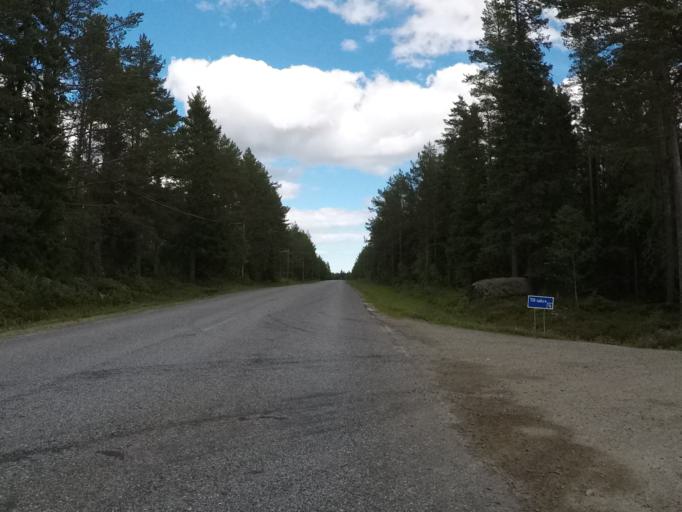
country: SE
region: Vaesterbotten
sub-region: Umea Kommun
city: Saevar
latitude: 63.9254
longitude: 20.7730
